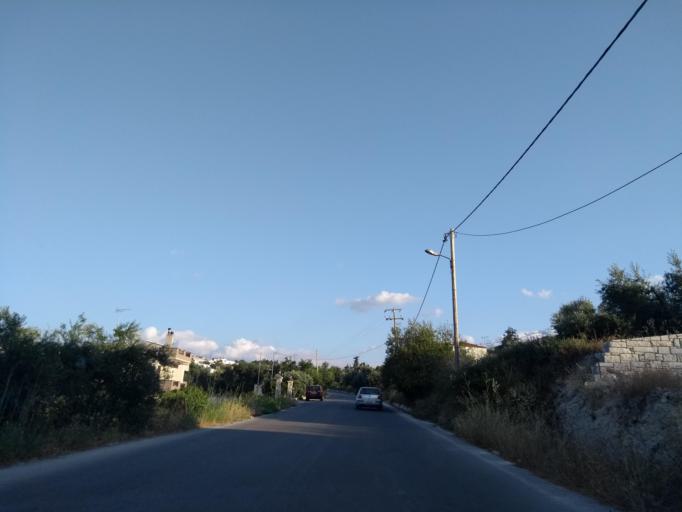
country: GR
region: Crete
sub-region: Nomos Chanias
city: Kalivai
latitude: 35.4399
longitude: 24.1753
